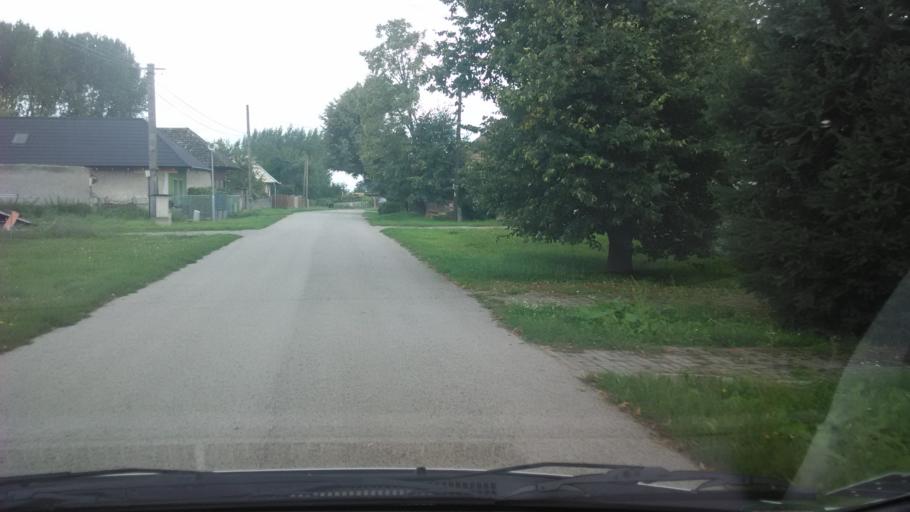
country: SK
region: Nitriansky
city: Levice
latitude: 48.1953
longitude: 18.5226
